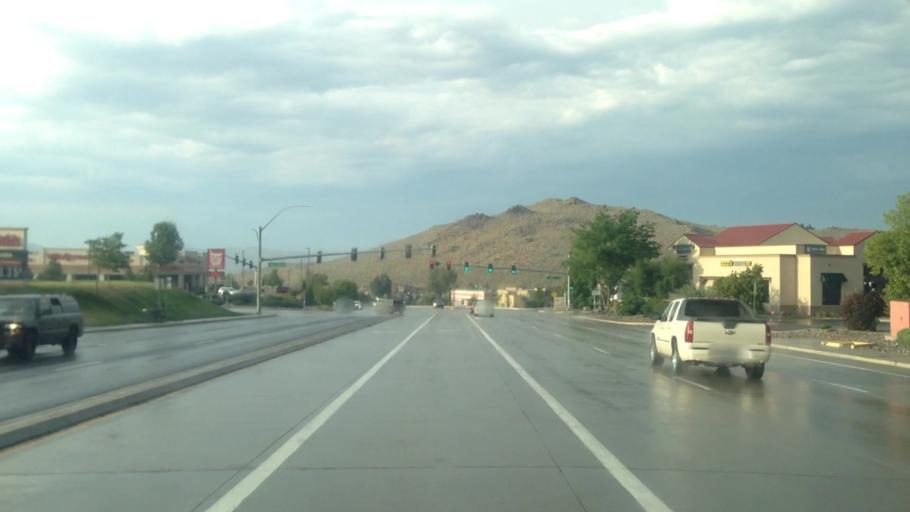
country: US
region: Nevada
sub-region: Washoe County
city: Golden Valley
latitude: 39.6130
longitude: -119.8497
